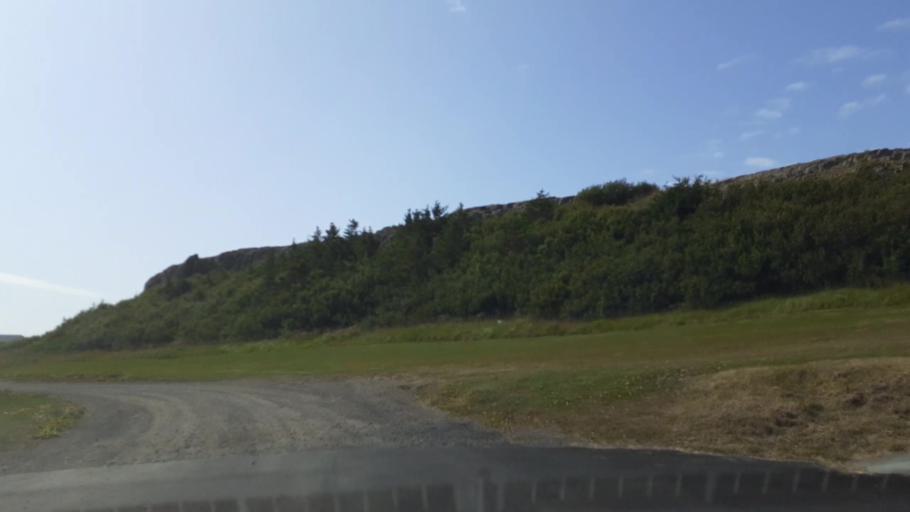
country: IS
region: Northwest
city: Saudarkrokur
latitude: 65.8287
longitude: -20.3207
